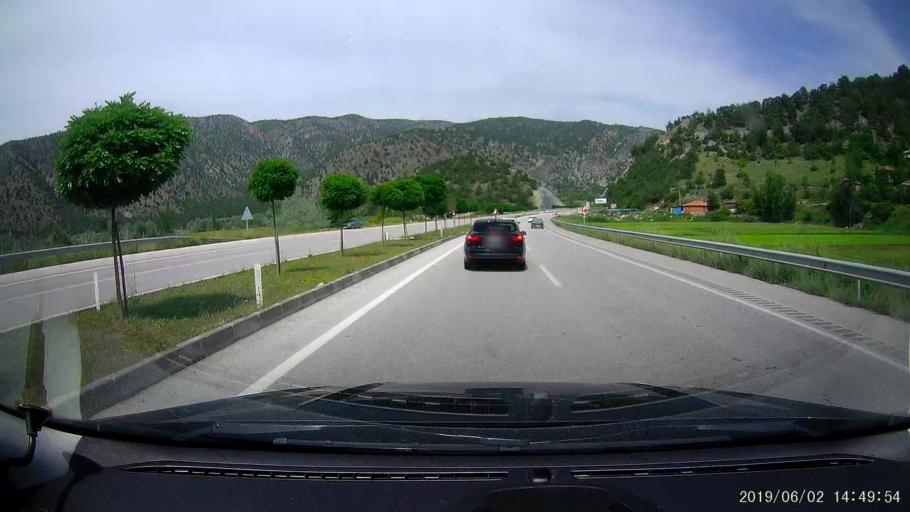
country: TR
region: Corum
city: Hacihamza
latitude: 41.0705
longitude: 34.5083
